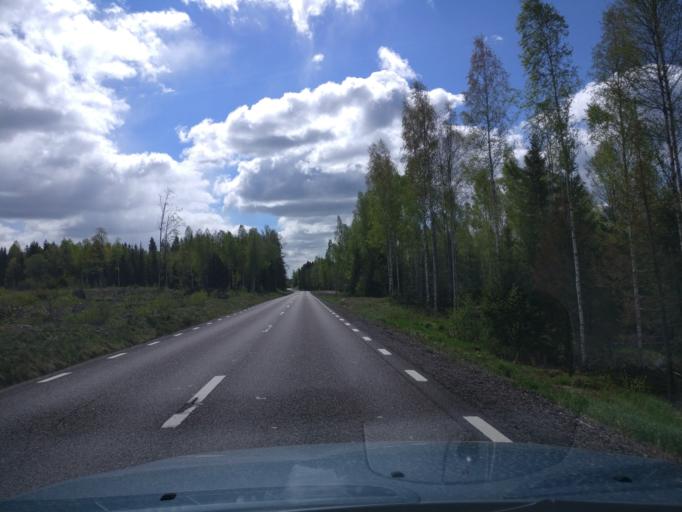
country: SE
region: Vaermland
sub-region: Karlstads Kommun
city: Molkom
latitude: 59.7353
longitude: 13.6789
